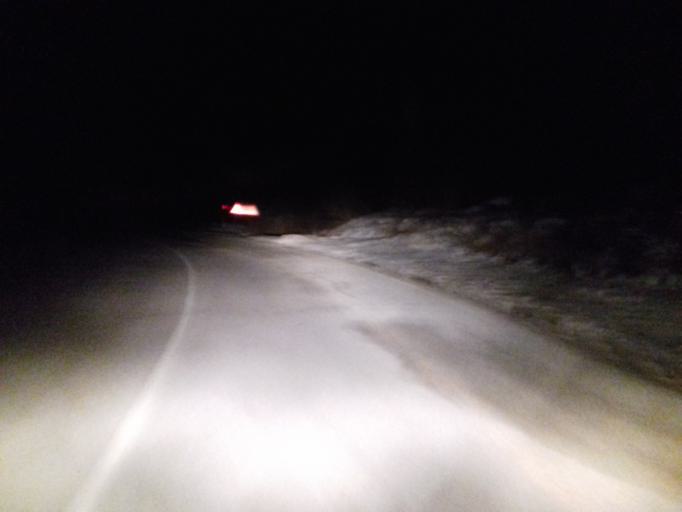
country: BA
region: Federation of Bosnia and Herzegovina
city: Gracanica
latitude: 43.7318
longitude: 18.3102
